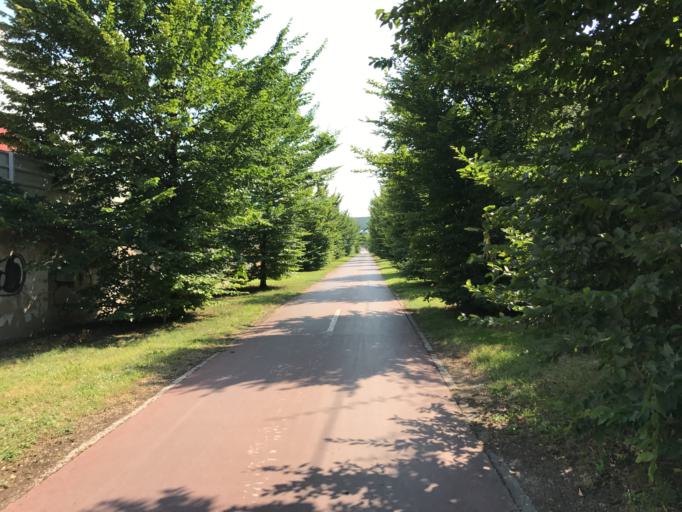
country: ES
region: Basque Country
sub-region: Provincia de Alava
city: Gasteiz / Vitoria
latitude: 42.8663
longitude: -2.6538
